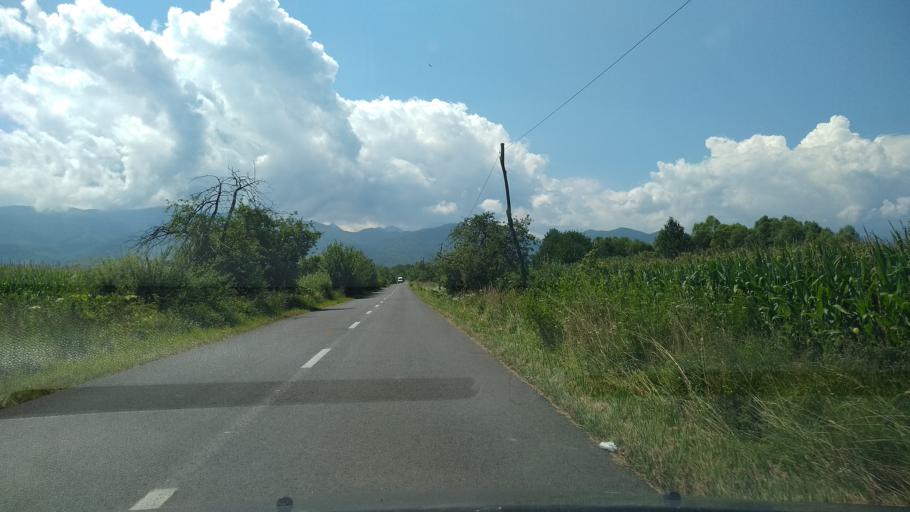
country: RO
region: Hunedoara
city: Salasu de Sus
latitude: 45.5203
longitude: 22.9611
